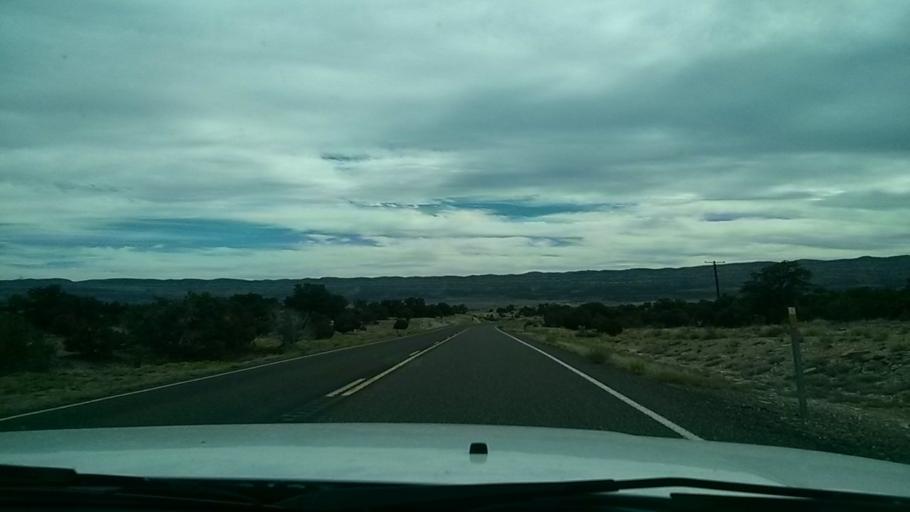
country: US
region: Utah
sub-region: Wayne County
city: Loa
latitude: 37.7291
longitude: -111.5203
